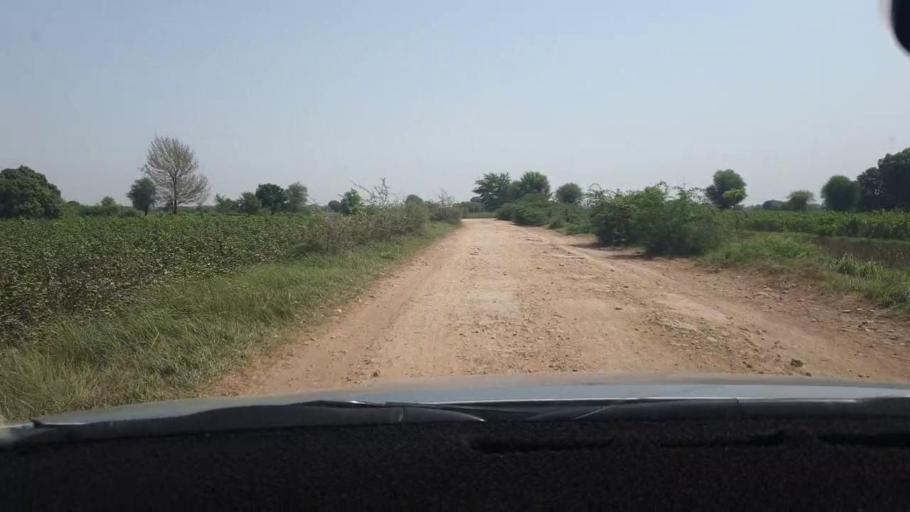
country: PK
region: Sindh
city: Tando Mittha Khan
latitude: 25.8462
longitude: 69.4345
